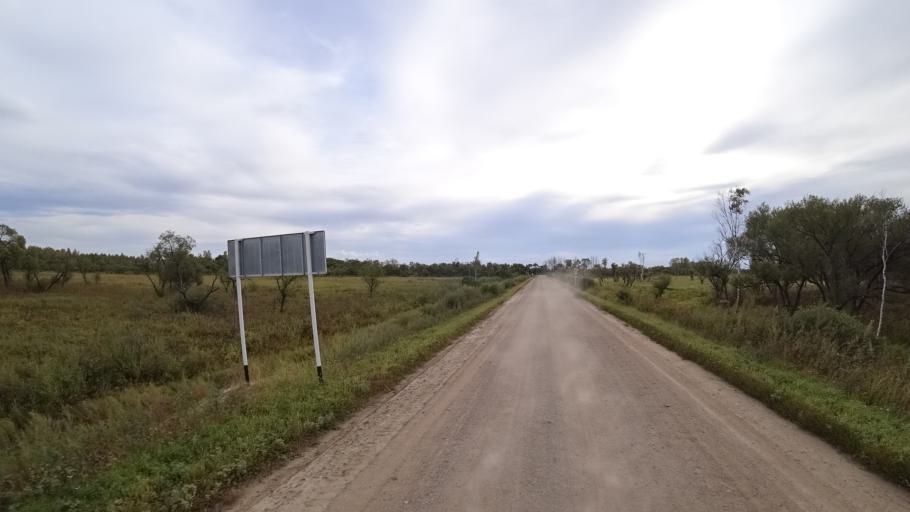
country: RU
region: Amur
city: Arkhara
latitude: 49.3754
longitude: 130.2081
